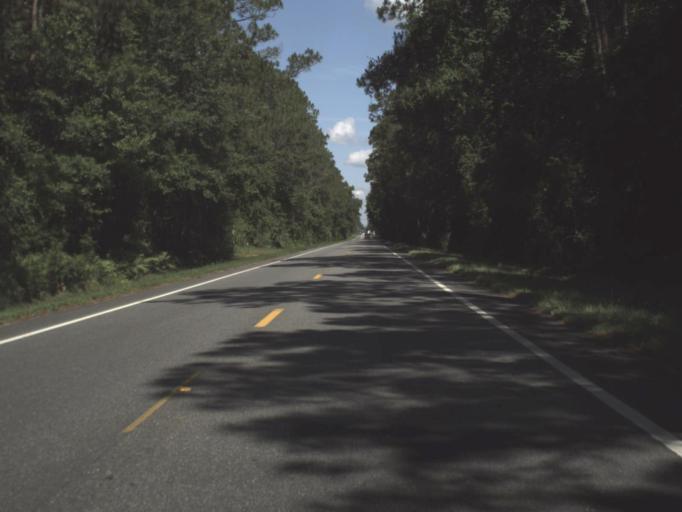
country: US
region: Florida
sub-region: Putnam County
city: Palatka
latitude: 29.6710
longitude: -81.7048
